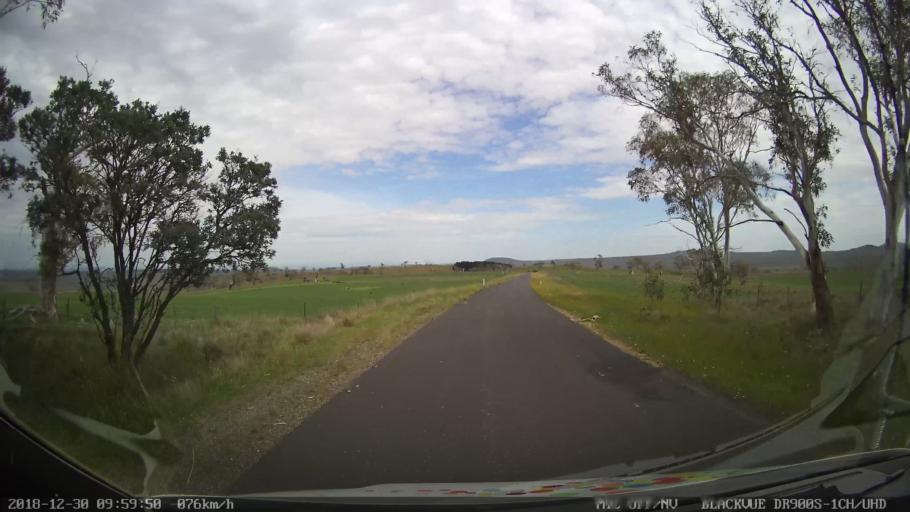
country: AU
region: New South Wales
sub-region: Cooma-Monaro
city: Cooma
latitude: -36.5210
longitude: 149.2050
